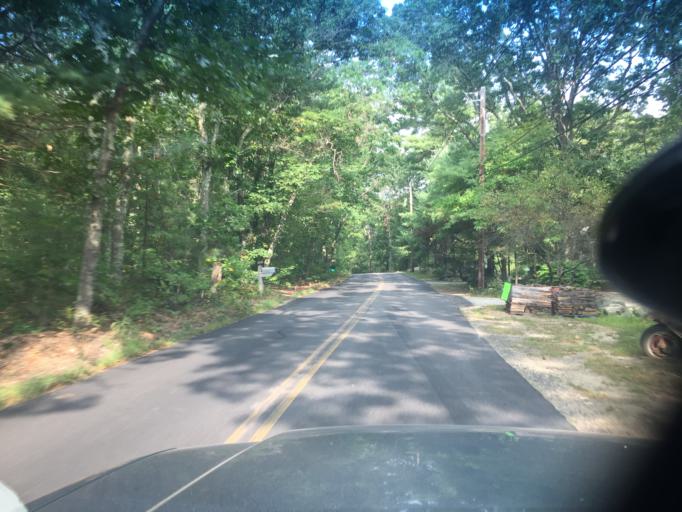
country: US
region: Massachusetts
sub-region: Norfolk County
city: Bellingham
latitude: 42.1308
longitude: -71.4603
